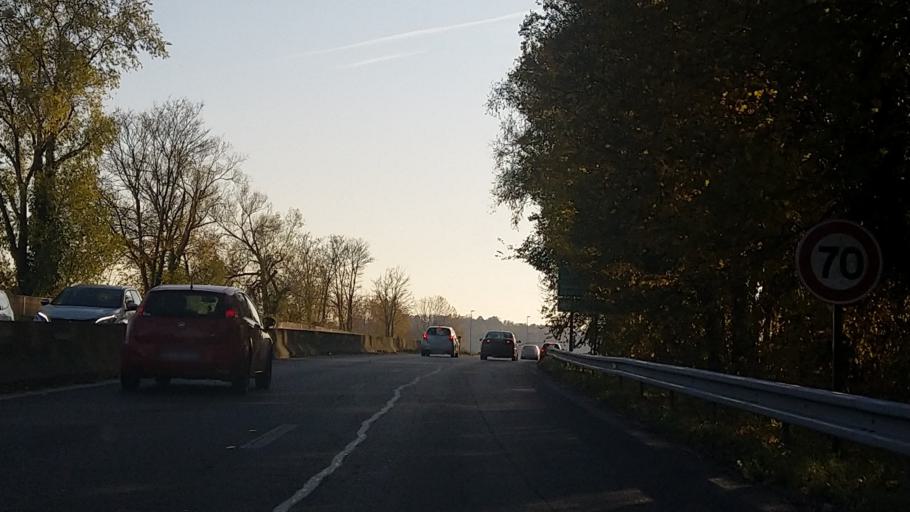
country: FR
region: Ile-de-France
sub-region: Departement du Val-d'Oise
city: Saint-Brice-sous-Foret
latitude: 48.9951
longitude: 2.3608
